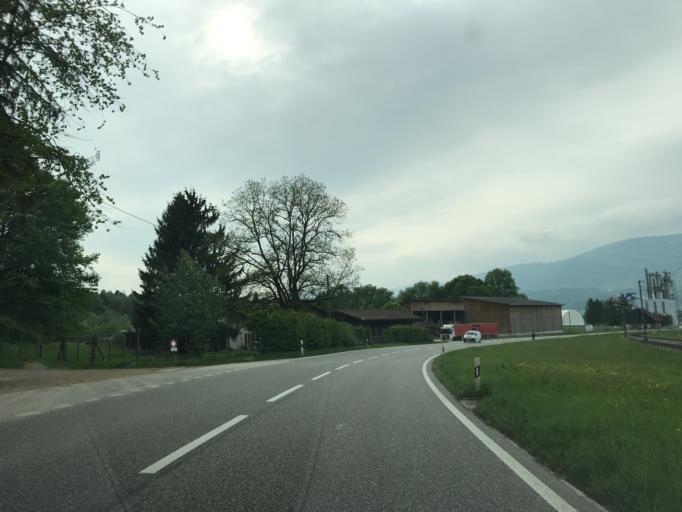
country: CH
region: Bern
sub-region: Oberaargau
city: Niederbipp
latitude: 47.2519
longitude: 7.7216
